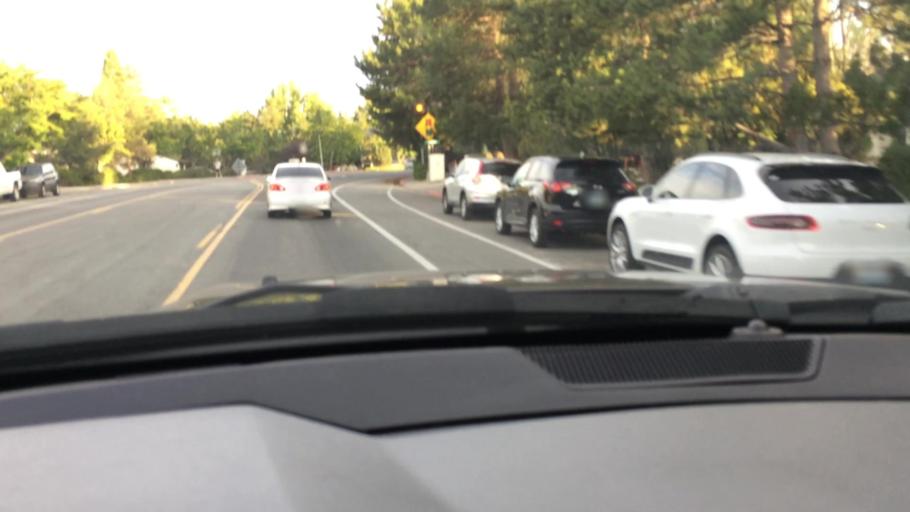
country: US
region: Nevada
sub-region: Washoe County
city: Reno
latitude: 39.4778
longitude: -119.8121
